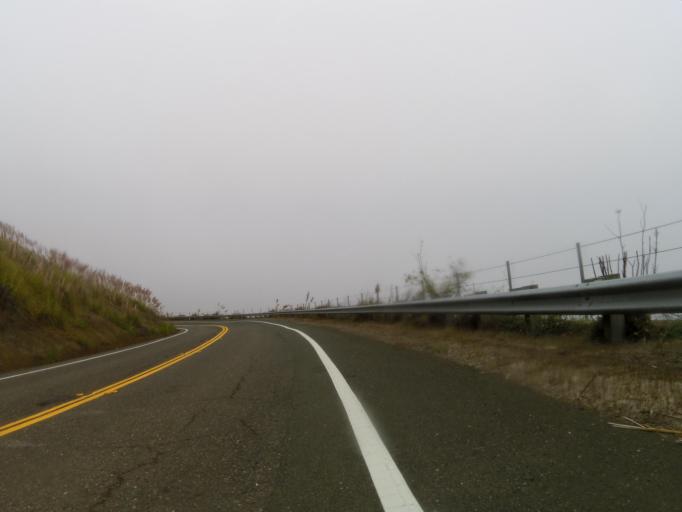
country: US
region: California
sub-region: Sonoma County
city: Monte Rio
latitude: 38.4800
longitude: -123.1690
